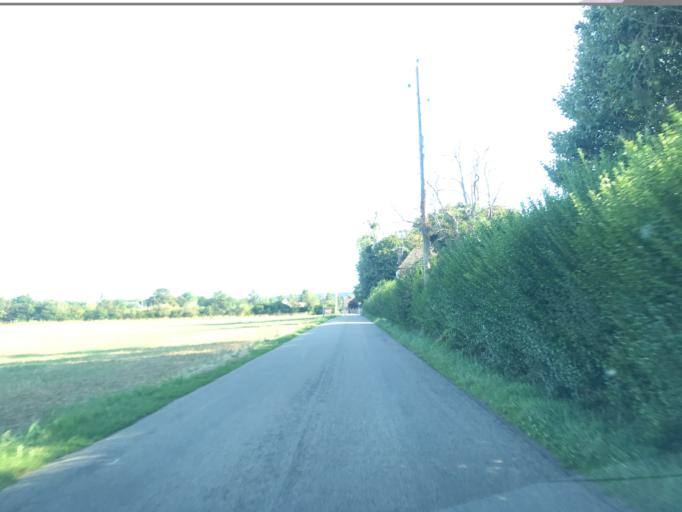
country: FR
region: Haute-Normandie
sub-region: Departement de l'Eure
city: Houlbec-Cocherel
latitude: 49.0549
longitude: 1.2999
